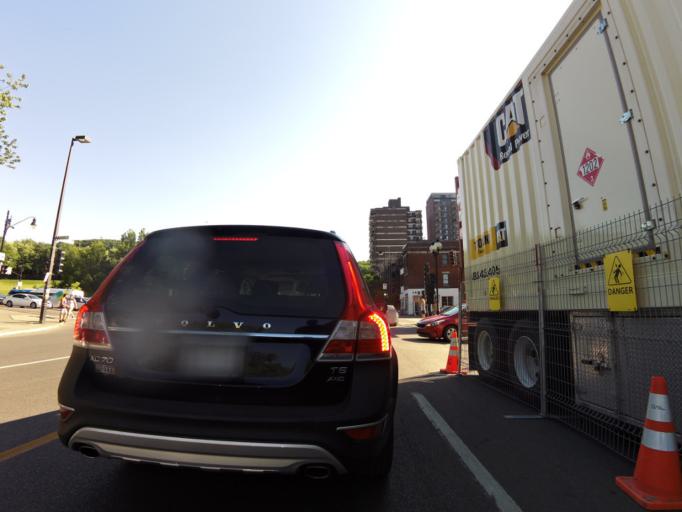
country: CA
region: Quebec
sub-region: Montreal
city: Montreal
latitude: 45.5172
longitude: -73.5892
